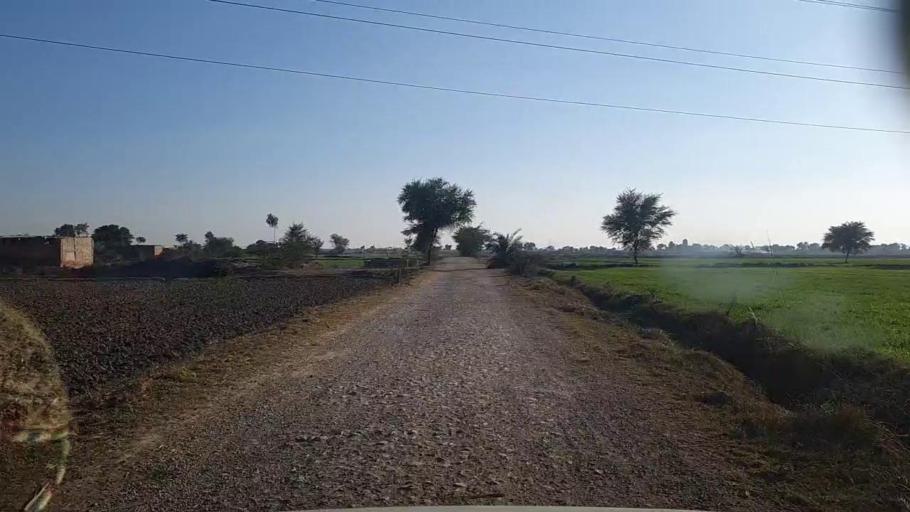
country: PK
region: Sindh
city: Khairpur
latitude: 28.0205
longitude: 69.7107
